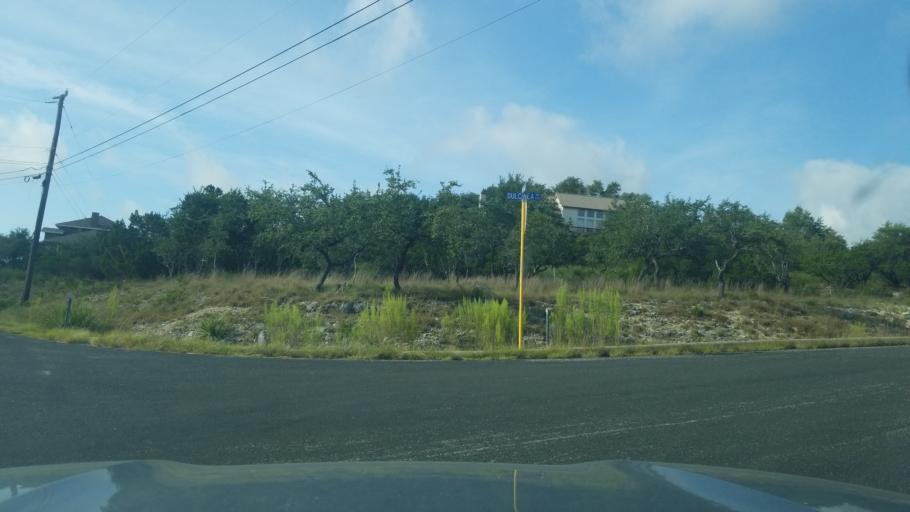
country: US
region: Texas
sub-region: Bexar County
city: Timberwood Park
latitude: 29.6876
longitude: -98.5040
